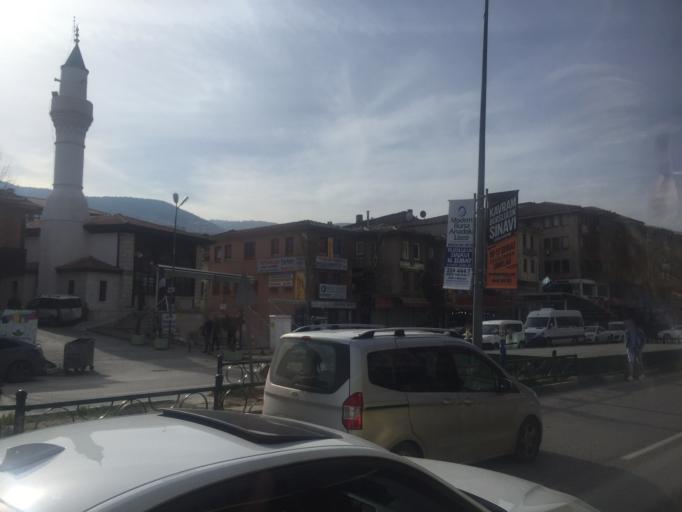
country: TR
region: Bursa
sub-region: Osmangazi
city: Bursa
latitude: 40.1883
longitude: 29.0640
